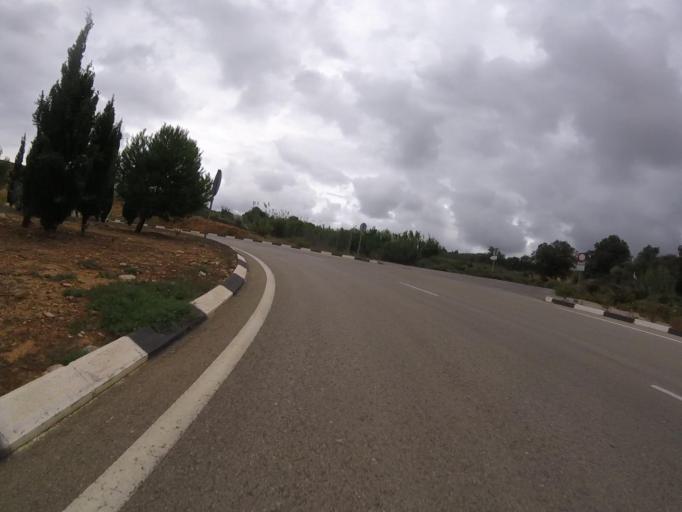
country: ES
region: Valencia
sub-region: Provincia de Castello
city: Benlloch
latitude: 40.1955
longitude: 0.0535
